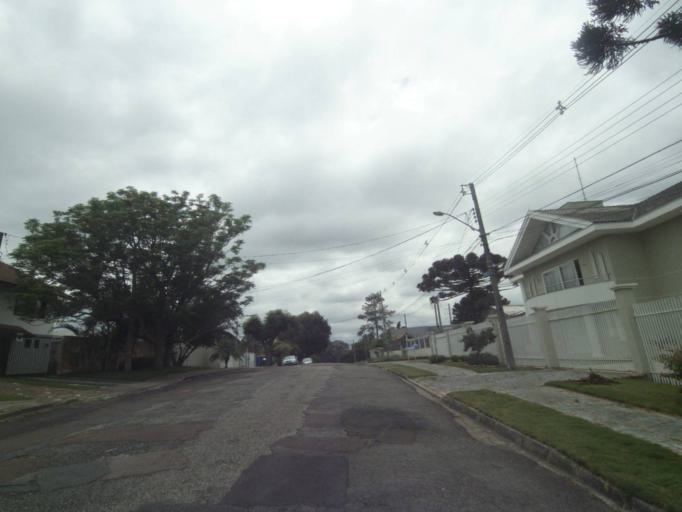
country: BR
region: Parana
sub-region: Curitiba
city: Curitiba
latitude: -25.3891
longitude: -49.2735
